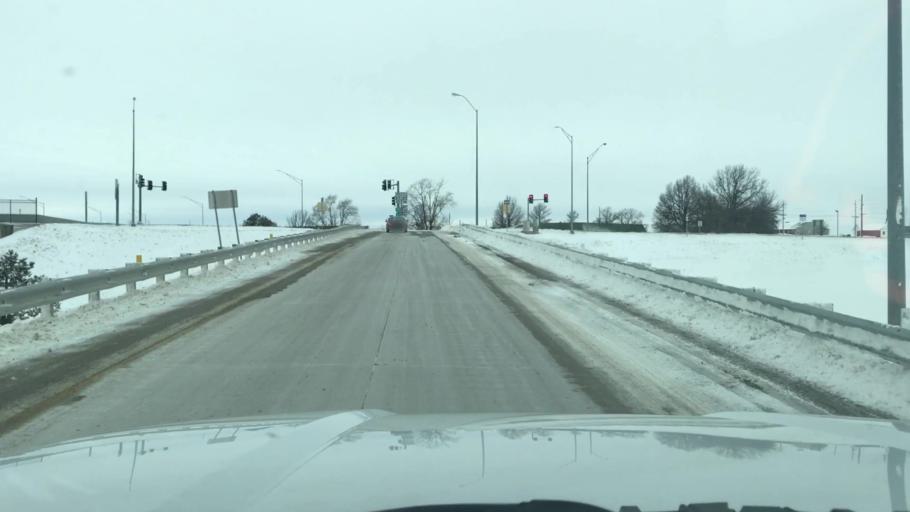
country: US
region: Missouri
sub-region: Clinton County
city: Cameron
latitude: 39.7550
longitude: -94.2331
